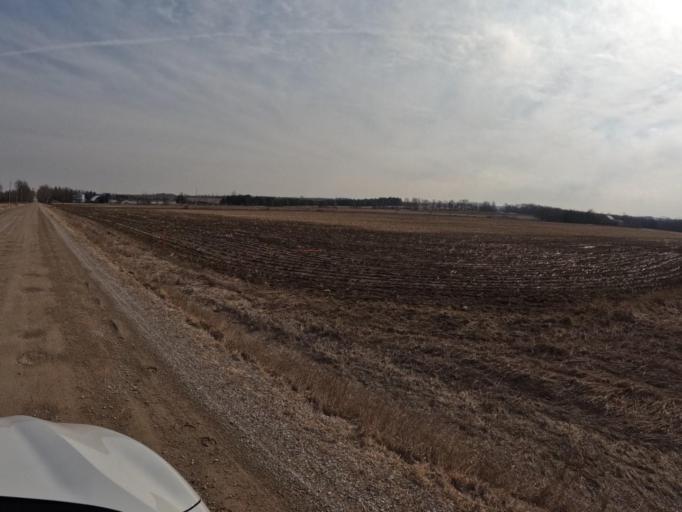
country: CA
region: Ontario
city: Orangeville
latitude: 43.9040
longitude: -80.2687
